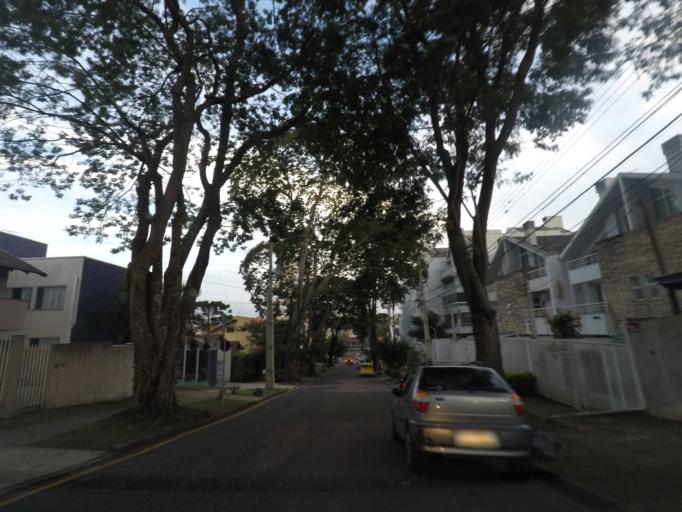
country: BR
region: Parana
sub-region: Curitiba
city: Curitiba
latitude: -25.4203
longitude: -49.2775
